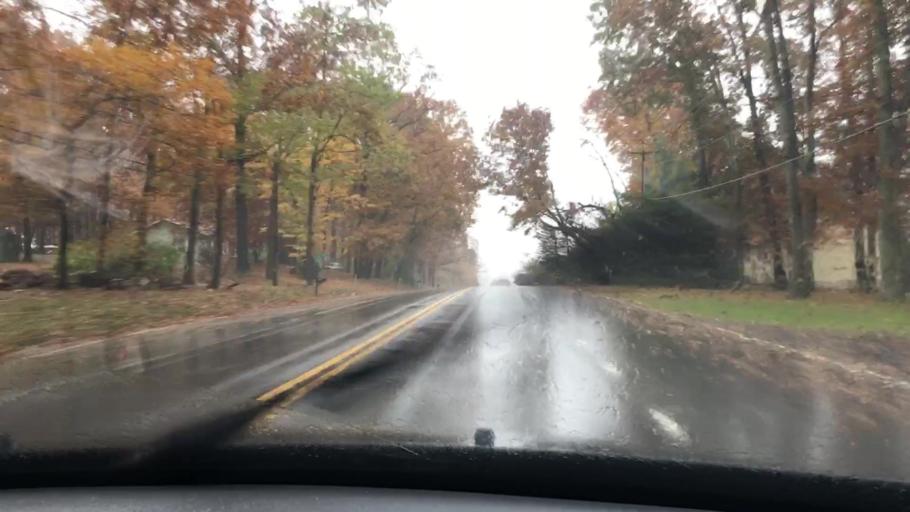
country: US
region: Maryland
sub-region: Carroll County
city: New Windsor
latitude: 39.4766
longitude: -77.0712
